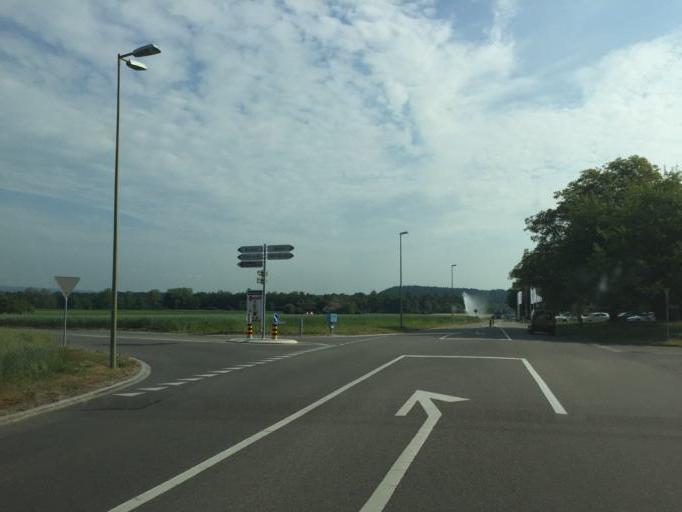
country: CH
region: Zurich
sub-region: Bezirk Buelach
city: Freienstein
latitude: 47.5787
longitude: 8.6113
